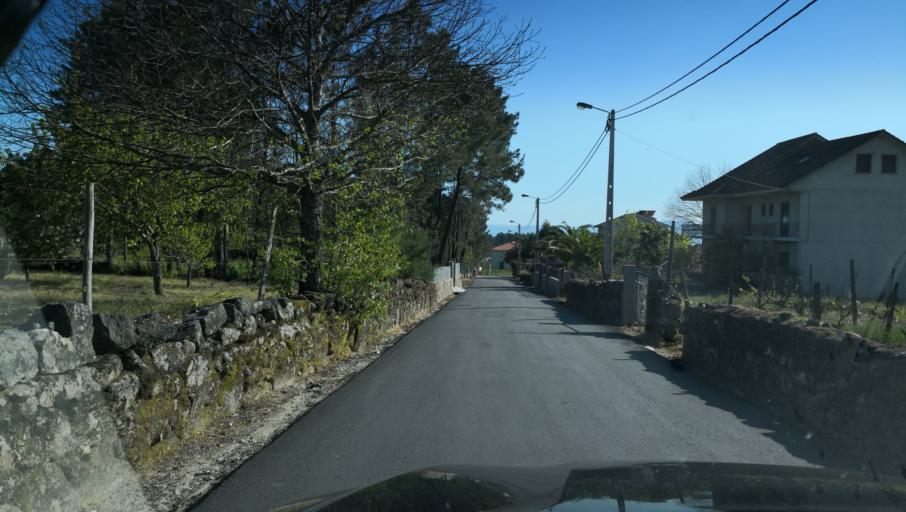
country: PT
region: Vila Real
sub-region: Vila Real
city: Vila Real
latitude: 41.2879
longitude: -7.6816
